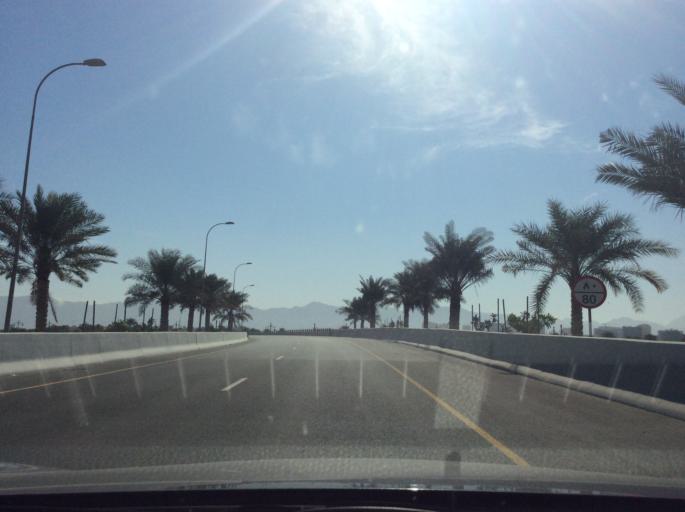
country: OM
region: Muhafazat Masqat
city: Bawshar
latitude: 23.5944
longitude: 58.3365
